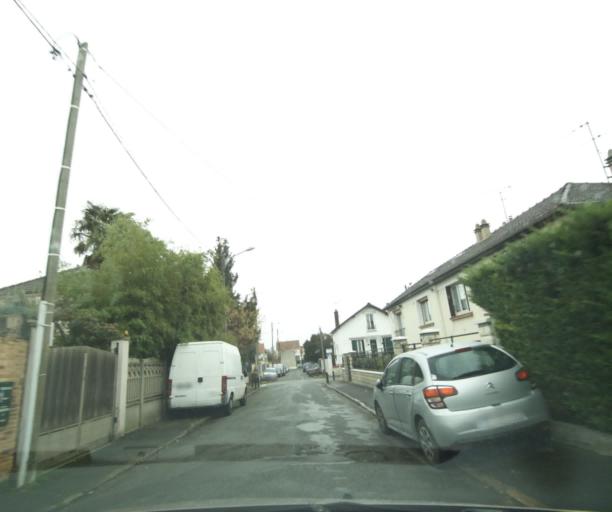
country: FR
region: Ile-de-France
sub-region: Departement du Val-de-Marne
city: Ablon-sur-Seine
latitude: 48.7402
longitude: 2.4211
